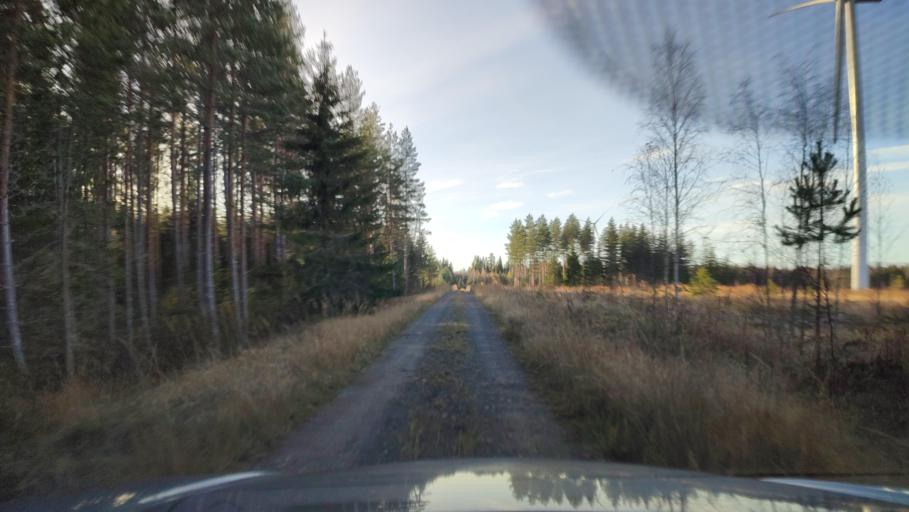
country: FI
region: Southern Ostrobothnia
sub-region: Suupohja
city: Karijoki
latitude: 62.1795
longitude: 21.6089
